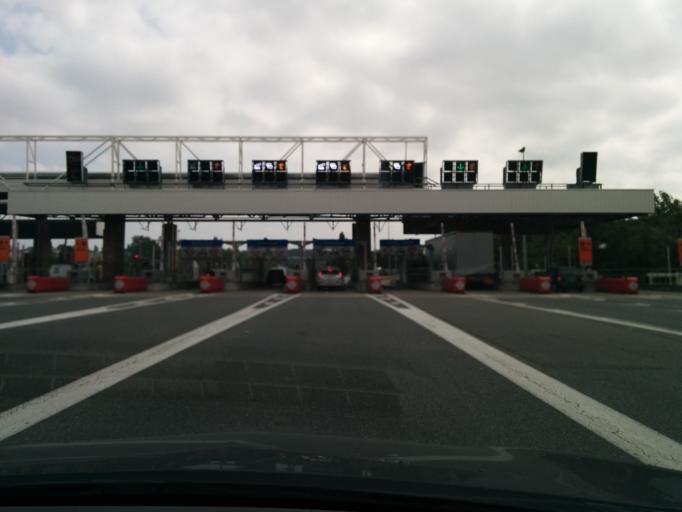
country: FR
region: Midi-Pyrenees
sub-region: Departement de la Haute-Garonne
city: Montrabe
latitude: 43.6469
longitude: 1.5071
